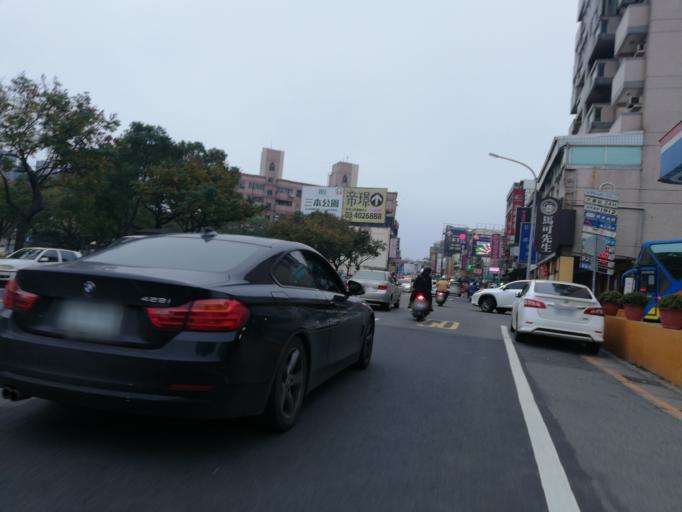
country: TW
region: Taiwan
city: Taoyuan City
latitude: 24.9802
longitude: 121.3053
